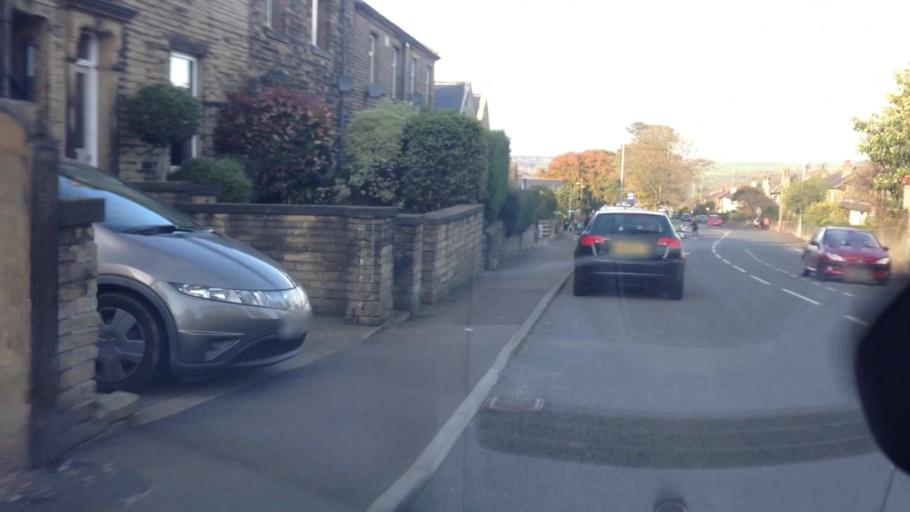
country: GB
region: England
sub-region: Calderdale
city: Brighouse
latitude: 53.6865
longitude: -1.7959
